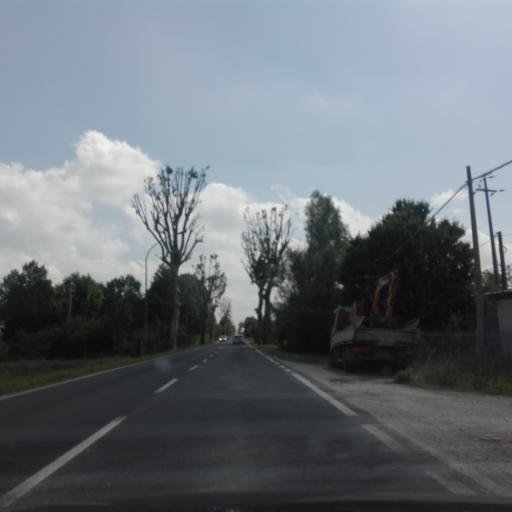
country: IT
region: Veneto
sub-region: Provincia di Rovigo
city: Buso
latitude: 45.0758
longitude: 11.8307
